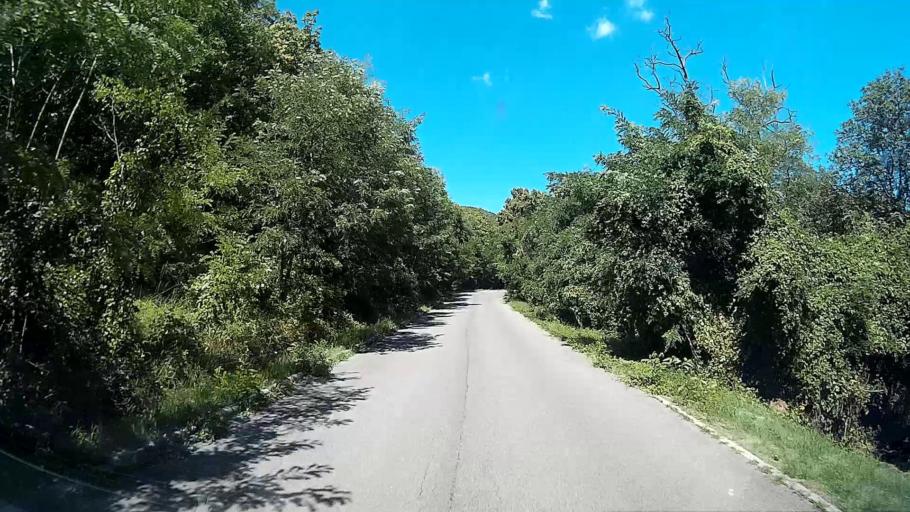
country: HU
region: Pest
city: Leanyfalu
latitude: 47.7016
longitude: 19.0745
